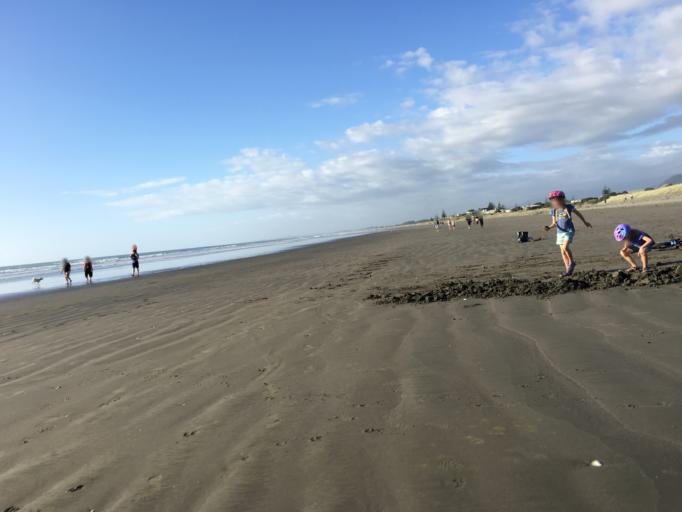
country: NZ
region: Wellington
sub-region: Kapiti Coast District
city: Paraparaumu
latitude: -40.8596
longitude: 175.0244
